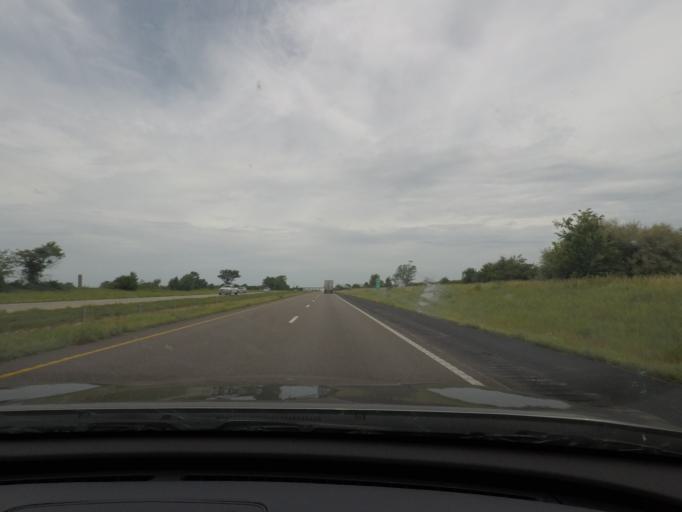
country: US
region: Missouri
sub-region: Callaway County
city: Fulton
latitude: 38.9152
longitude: -91.7368
